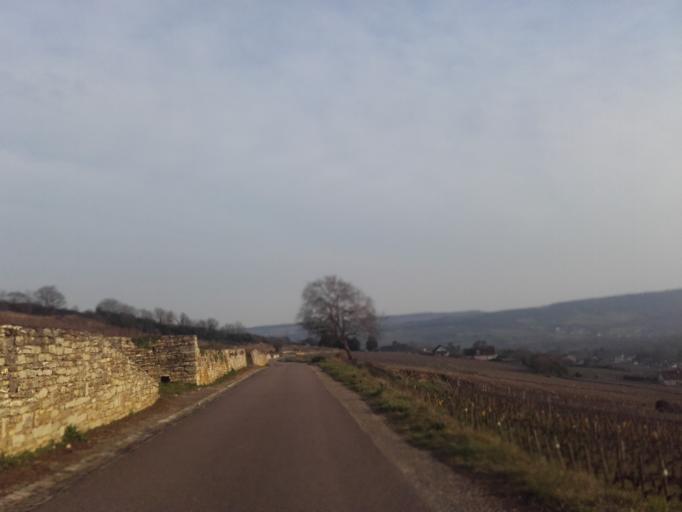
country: FR
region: Bourgogne
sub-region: Departement de la Cote-d'Or
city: Nolay
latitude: 46.9183
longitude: 4.6803
